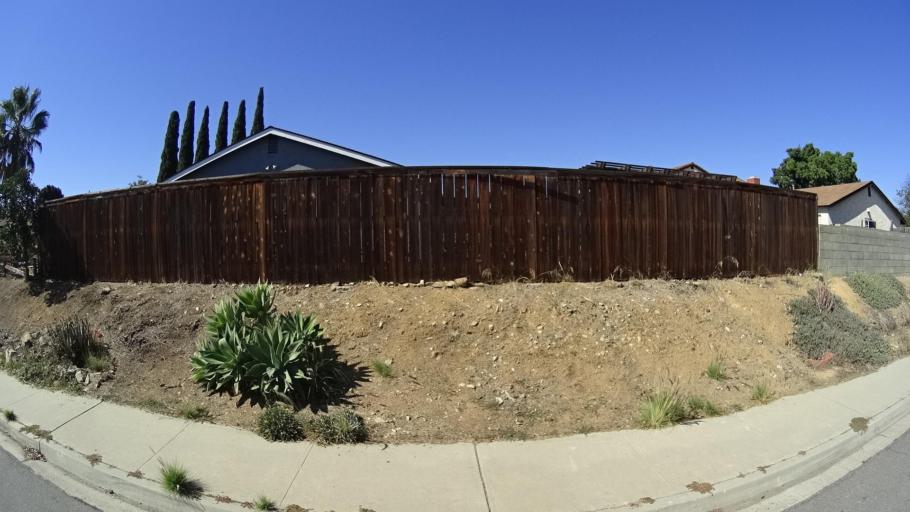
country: US
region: California
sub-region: San Diego County
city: La Presa
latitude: 32.6965
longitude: -117.0049
